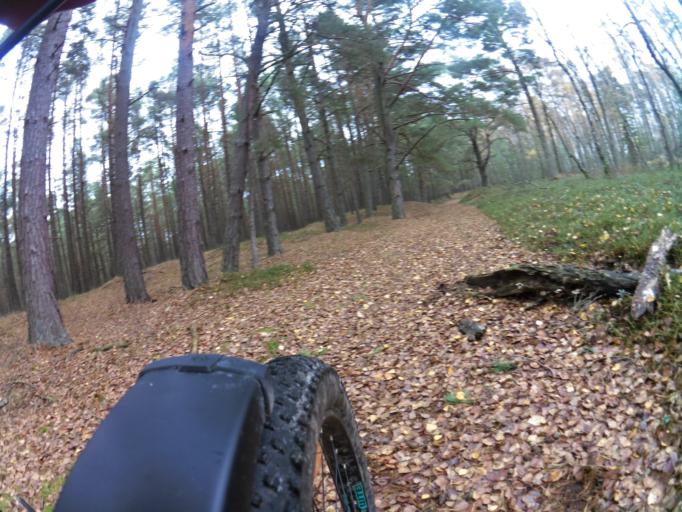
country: PL
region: Pomeranian Voivodeship
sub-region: Powiat leborski
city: Leba
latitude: 54.7676
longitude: 17.6092
